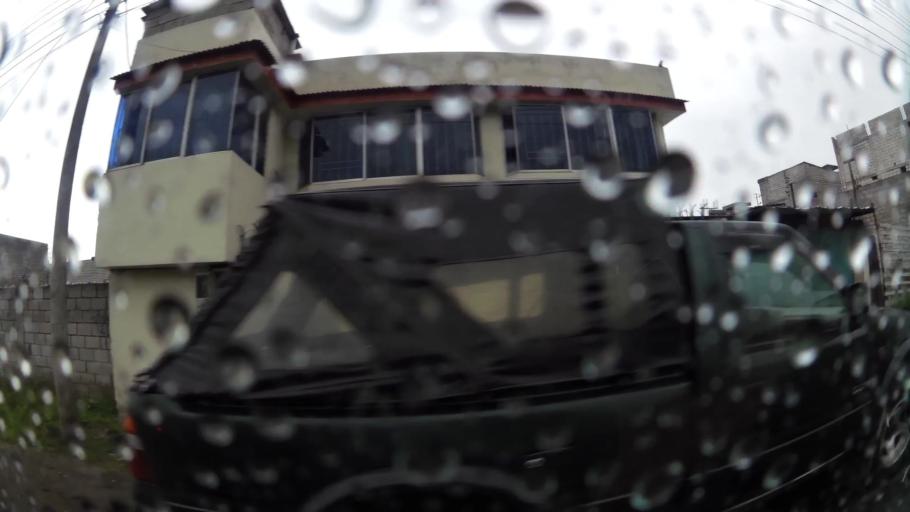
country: EC
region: Pichincha
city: Quito
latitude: -0.3197
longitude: -78.5561
